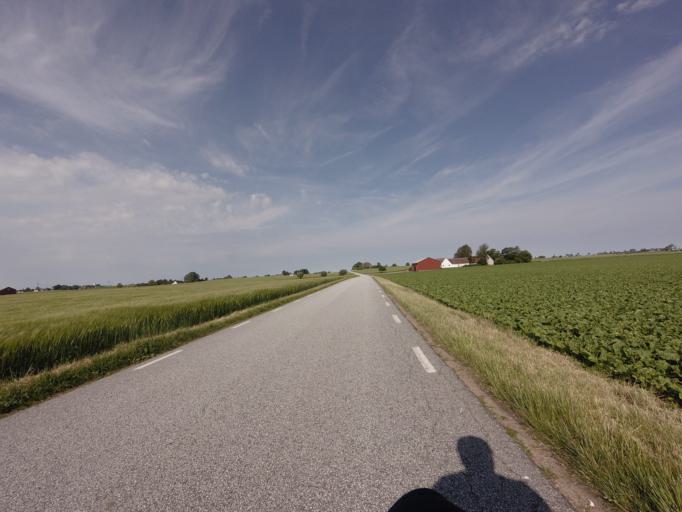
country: SE
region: Skane
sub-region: Malmo
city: Oxie
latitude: 55.4955
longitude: 13.0729
